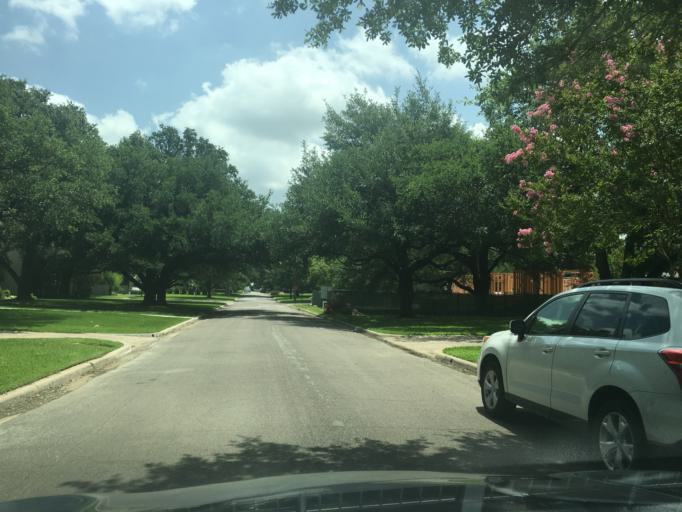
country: US
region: Texas
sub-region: Dallas County
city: University Park
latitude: 32.8746
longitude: -96.7924
